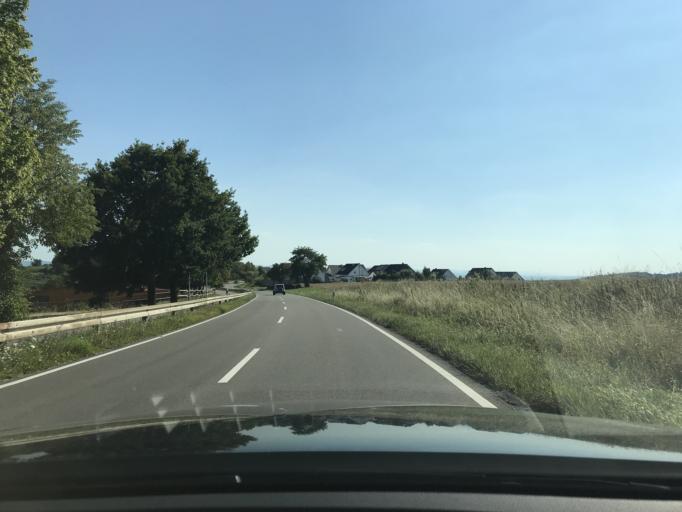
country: DE
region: Baden-Wuerttemberg
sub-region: Regierungsbezirk Stuttgart
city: Baltmannsweiler
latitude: 48.7420
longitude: 9.4808
